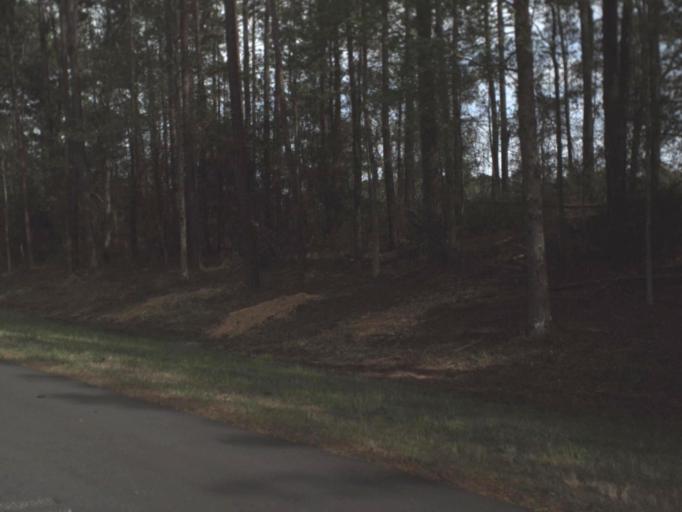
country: US
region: Florida
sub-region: Walton County
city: DeFuniak Springs
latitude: 30.6994
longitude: -85.9729
